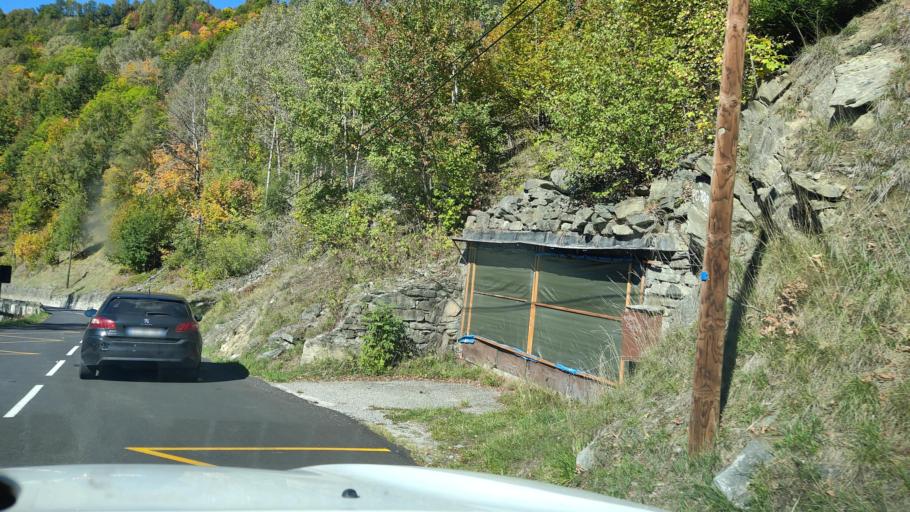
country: FR
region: Rhone-Alpes
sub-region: Departement de la Savoie
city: Seez
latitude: 45.6134
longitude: 6.8540
